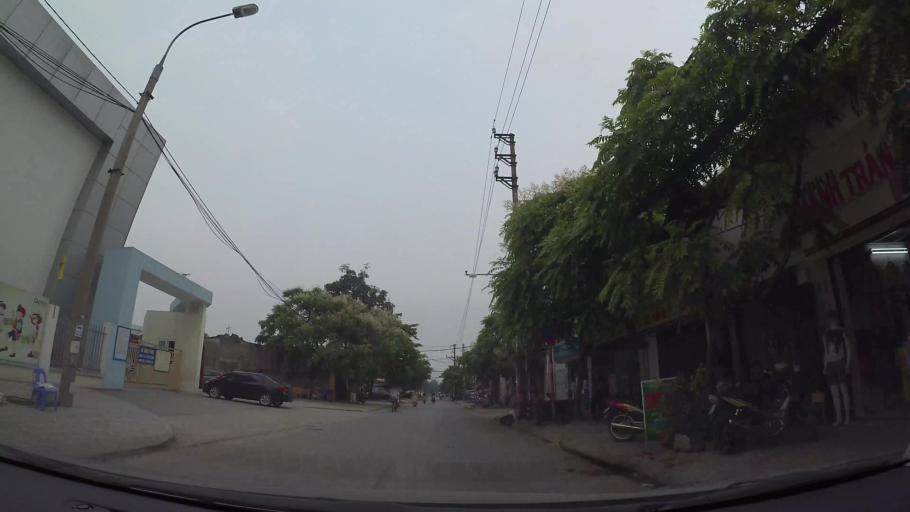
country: VN
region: Ha Noi
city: Hoan Kiem
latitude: 21.0686
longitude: 105.8892
